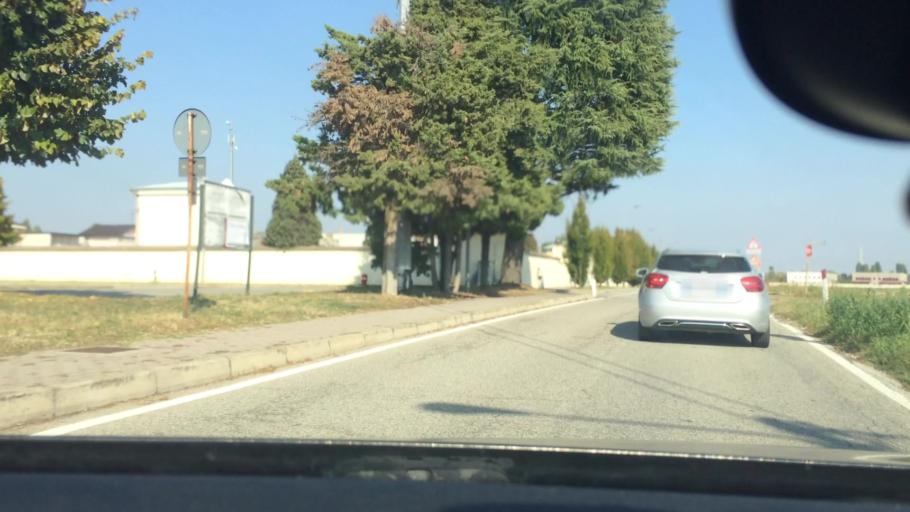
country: IT
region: Lombardy
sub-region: Citta metropolitana di Milano
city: Bernate Ticino
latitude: 45.4807
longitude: 8.8203
